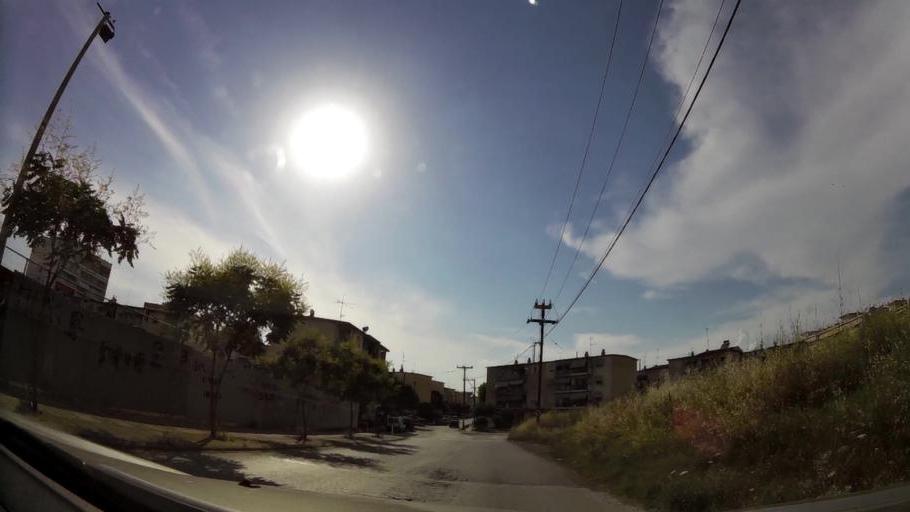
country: GR
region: Central Macedonia
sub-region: Nomos Thessalonikis
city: Kalamaria
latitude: 40.5670
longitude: 22.9646
